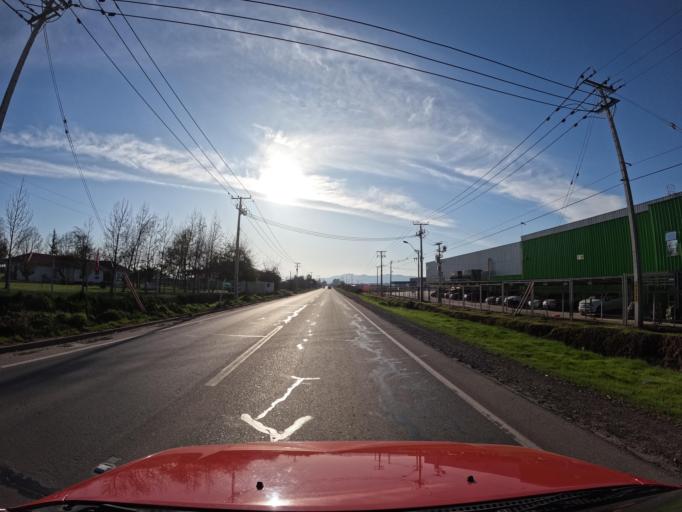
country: CL
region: Maule
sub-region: Provincia de Curico
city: Teno
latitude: -34.8556
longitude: -71.1045
